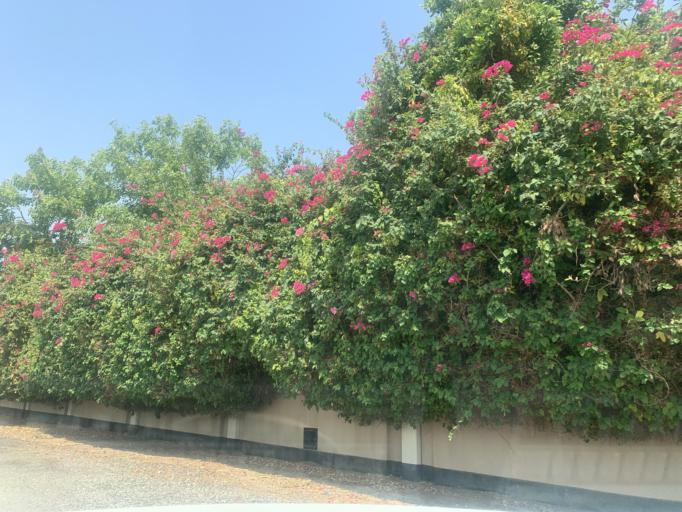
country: BH
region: Central Governorate
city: Madinat Hamad
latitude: 26.1667
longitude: 50.4586
